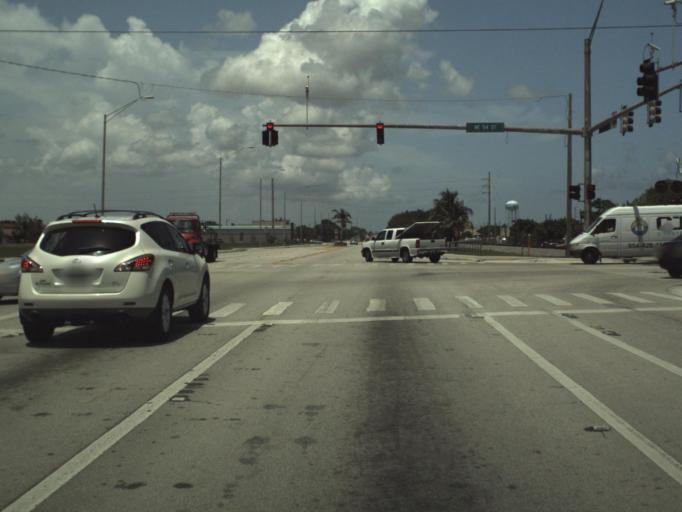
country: US
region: Florida
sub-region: Broward County
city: Pompano Beach Highlands
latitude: 26.2972
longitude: -80.1074
